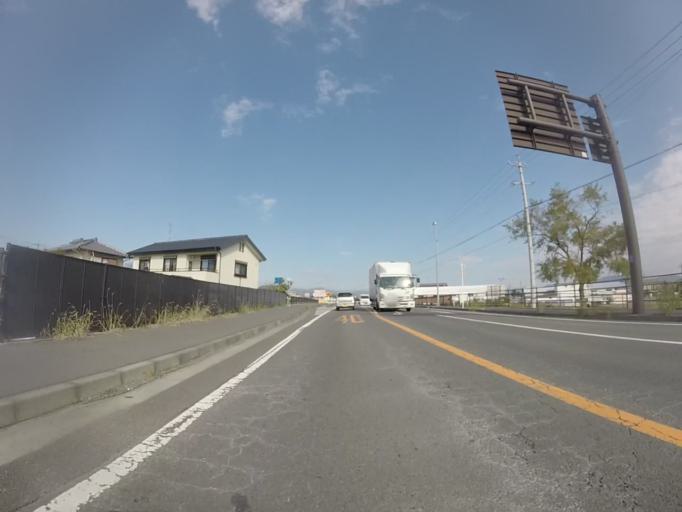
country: JP
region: Shizuoka
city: Fujieda
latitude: 34.8291
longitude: 138.2685
